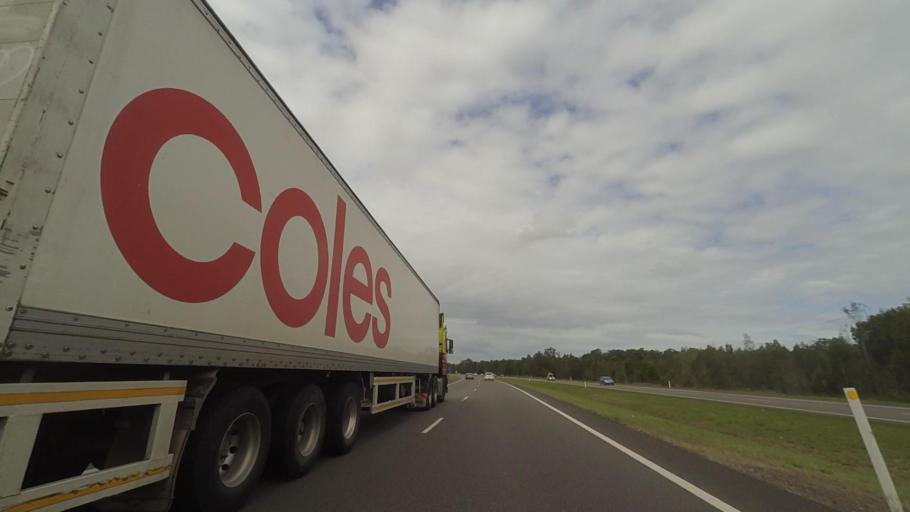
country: AU
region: New South Wales
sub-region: Port Stephens Shire
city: Raymond Terrace
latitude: -32.7768
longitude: 151.7543
